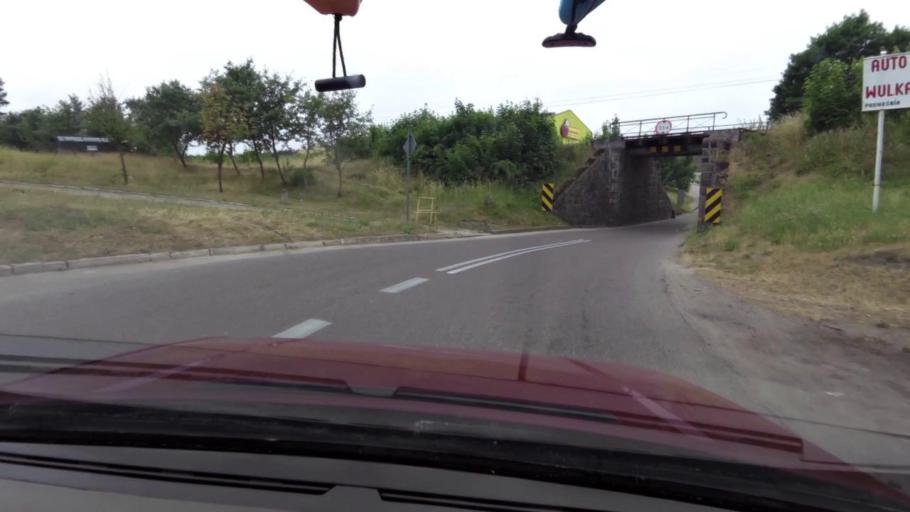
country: PL
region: Pomeranian Voivodeship
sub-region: Powiat slupski
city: Kepice
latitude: 54.2385
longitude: 16.8918
